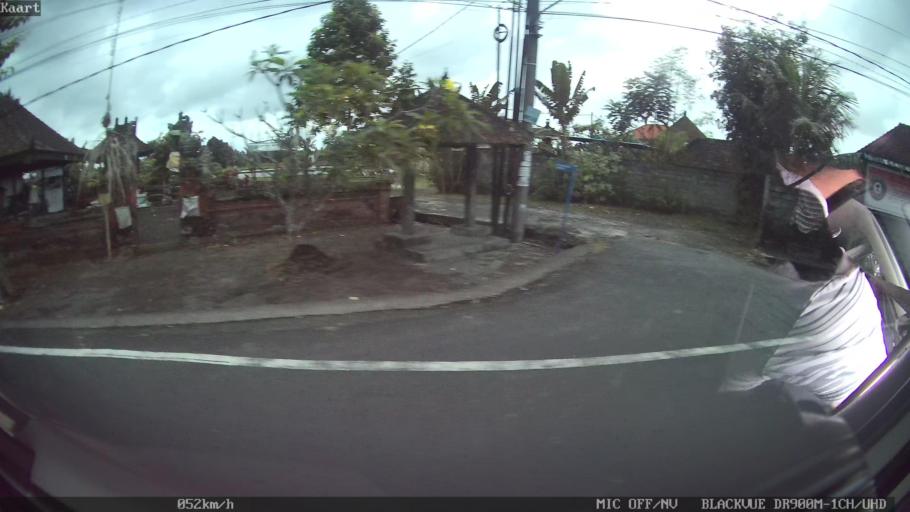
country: ID
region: Bali
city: Banjar Mambalkajanan
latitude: -8.5410
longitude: 115.2233
